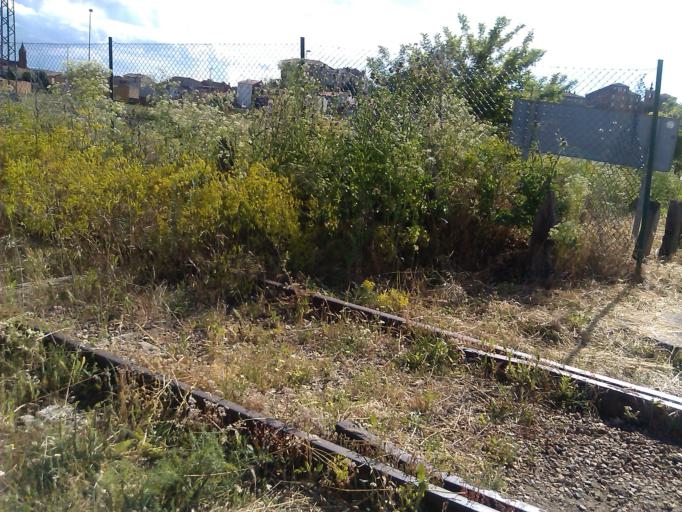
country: ES
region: Castille and Leon
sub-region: Provincia de Leon
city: Astorga
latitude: 42.4548
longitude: -6.0472
